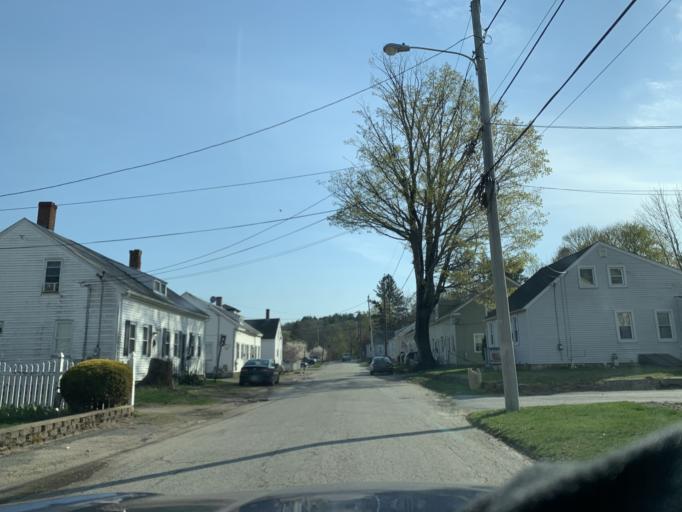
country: US
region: Rhode Island
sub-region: Kent County
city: West Warwick
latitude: 41.7268
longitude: -71.5359
